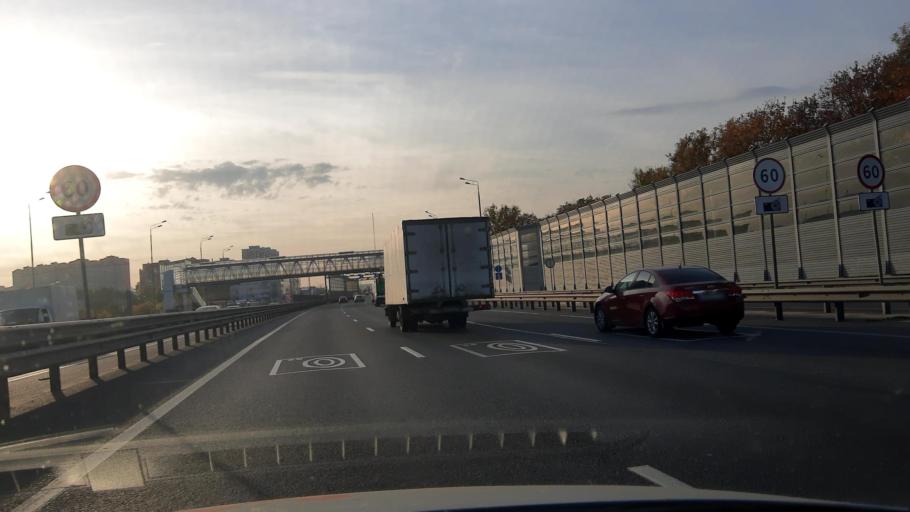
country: RU
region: Moskovskaya
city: Balashikha
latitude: 55.7957
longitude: 37.9490
